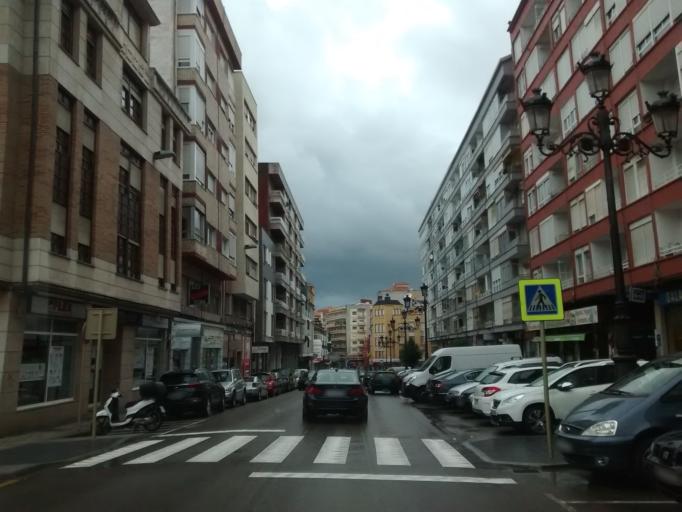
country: ES
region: Cantabria
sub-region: Provincia de Cantabria
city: Torrelavega
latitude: 43.3479
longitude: -4.0456
